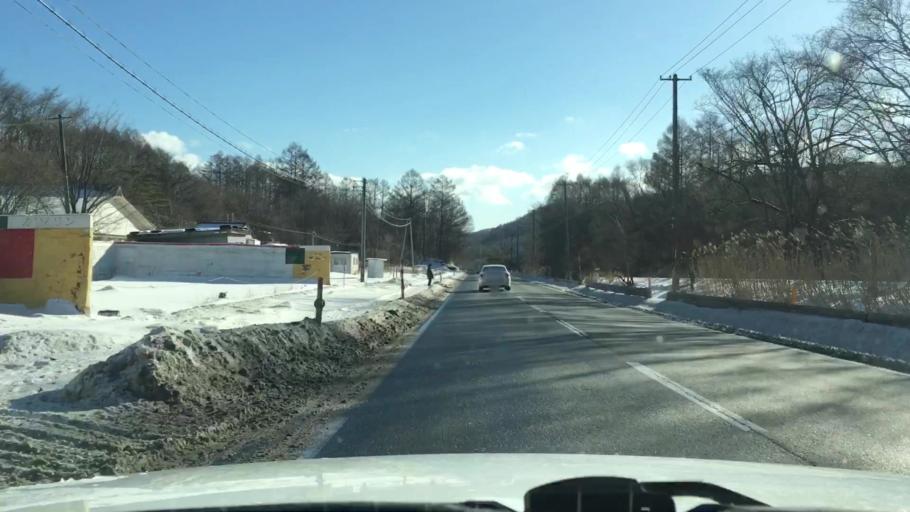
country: JP
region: Iwate
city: Morioka-shi
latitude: 39.6426
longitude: 141.4024
